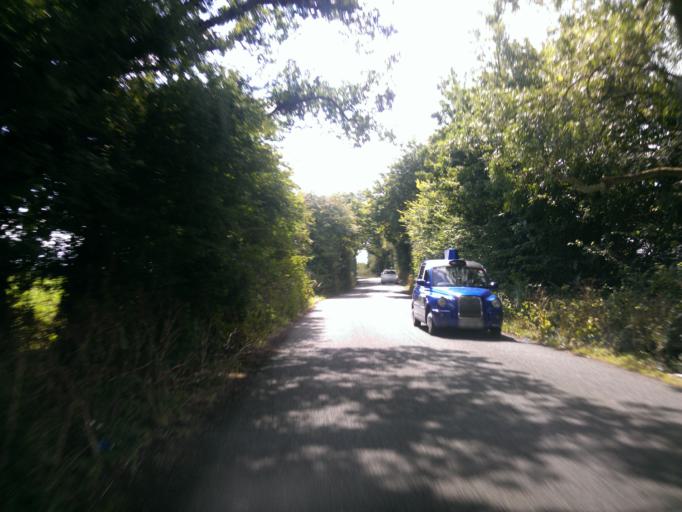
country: GB
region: England
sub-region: Essex
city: Saint Osyth
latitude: 51.7928
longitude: 1.0861
